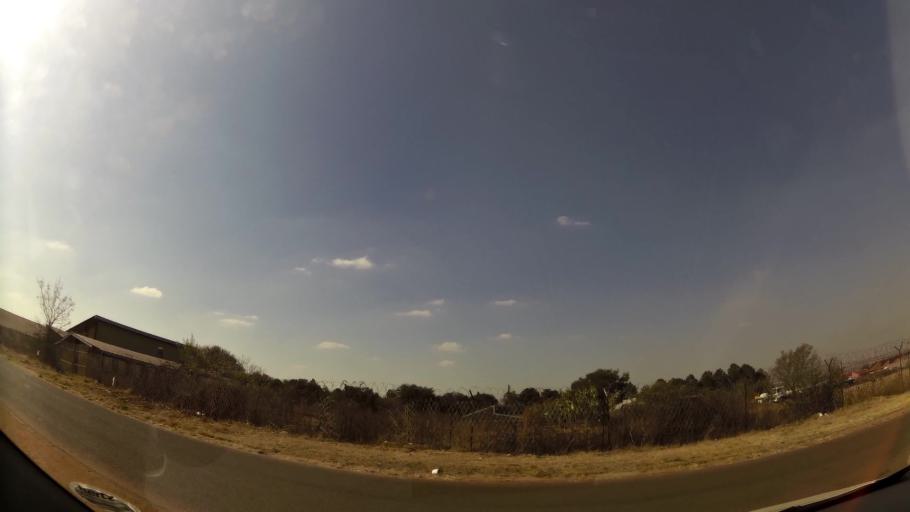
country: ZA
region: Gauteng
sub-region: City of Johannesburg Metropolitan Municipality
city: Roodepoort
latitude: -26.1647
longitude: 27.8011
